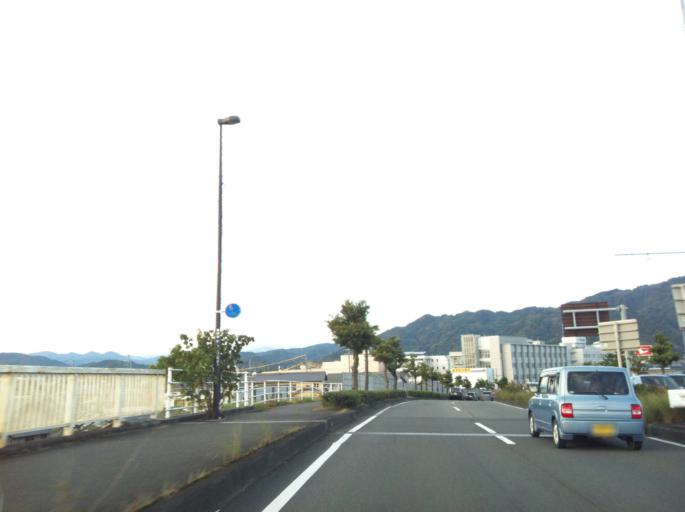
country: JP
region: Shizuoka
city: Yaizu
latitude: 34.8726
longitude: 138.2991
